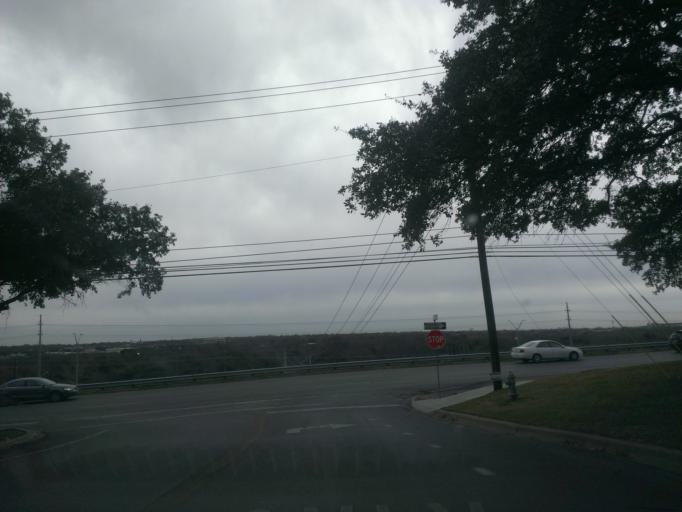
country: US
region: Texas
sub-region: Travis County
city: West Lake Hills
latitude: 30.3568
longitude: -97.7473
